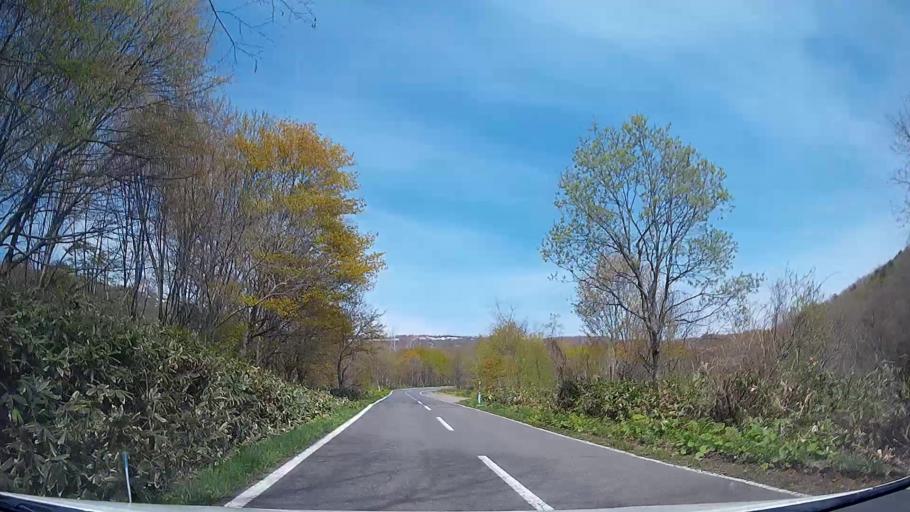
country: JP
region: Iwate
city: Shizukuishi
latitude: 39.9248
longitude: 140.9637
